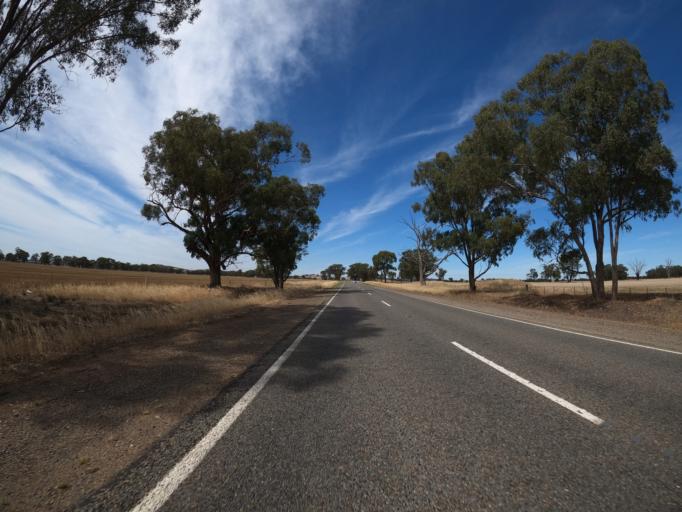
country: AU
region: Victoria
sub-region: Benalla
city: Benalla
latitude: -36.2960
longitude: 145.9523
